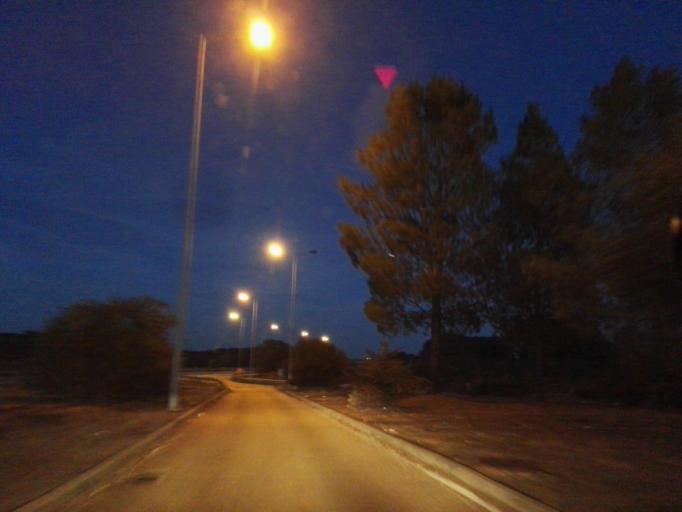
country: PT
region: Evora
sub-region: Estremoz
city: Estremoz
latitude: 38.7998
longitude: -7.6596
